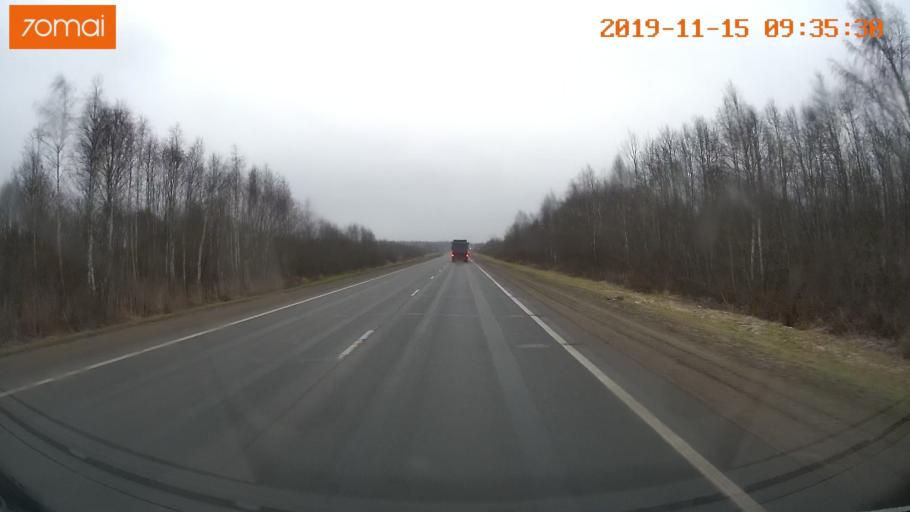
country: RU
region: Vologda
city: Sheksna
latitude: 59.2539
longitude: 38.4008
